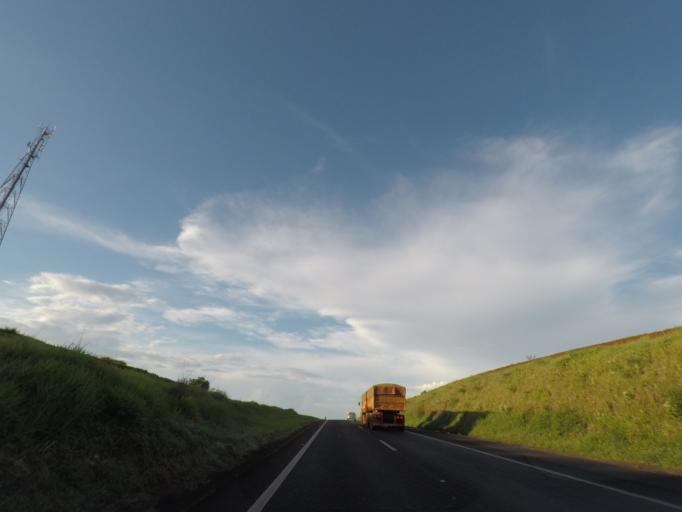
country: BR
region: Sao Paulo
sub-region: Ituverava
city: Ituverava
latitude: -20.2706
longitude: -47.7982
